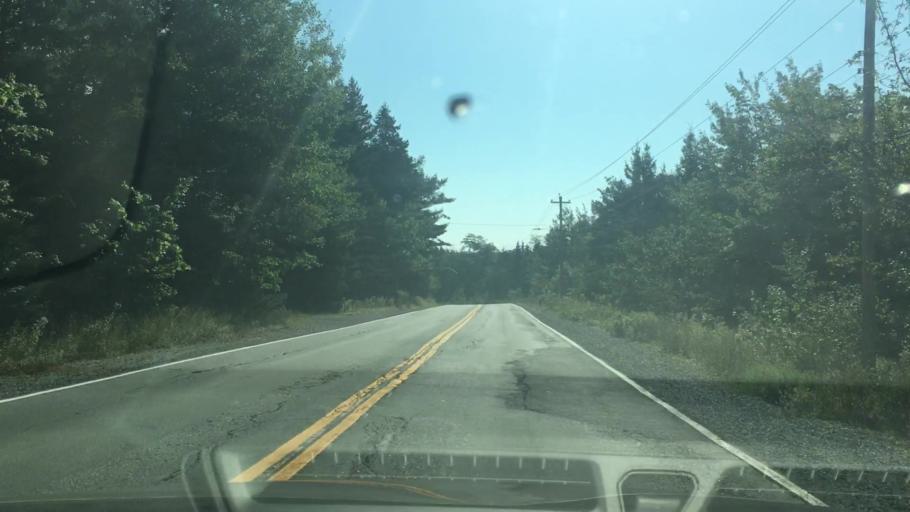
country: CA
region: Nova Scotia
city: Cole Harbour
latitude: 44.7774
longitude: -63.0733
